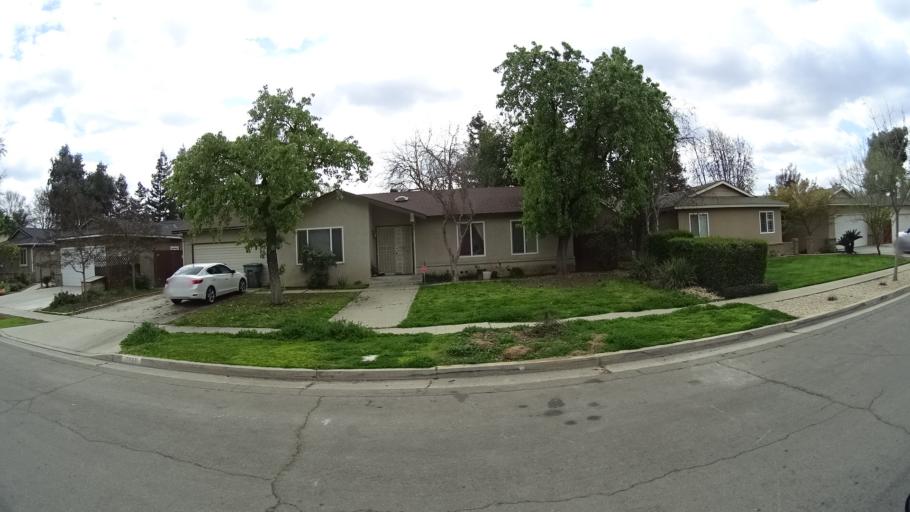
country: US
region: California
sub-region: Fresno County
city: Fresno
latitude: 36.8250
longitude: -119.8462
